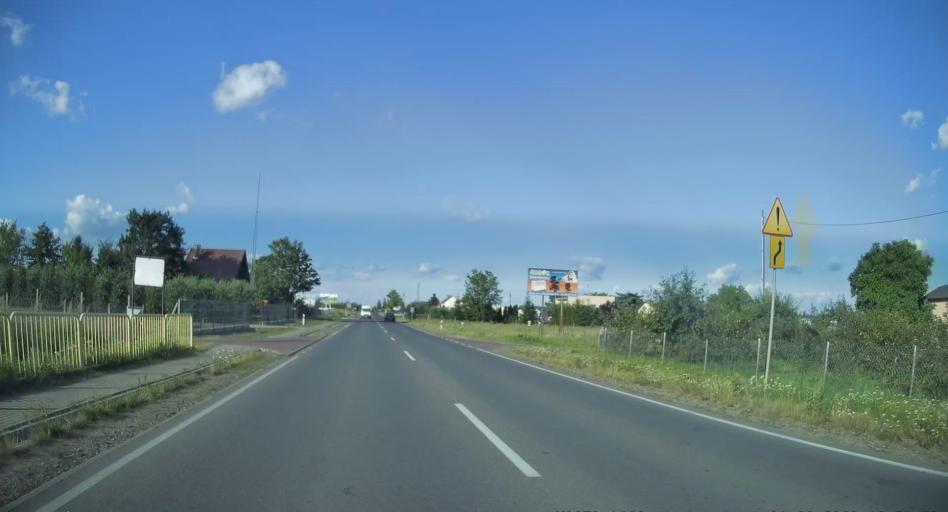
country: PL
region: Masovian Voivodeship
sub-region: Powiat grojecki
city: Grojec
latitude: 51.8505
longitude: 20.8412
